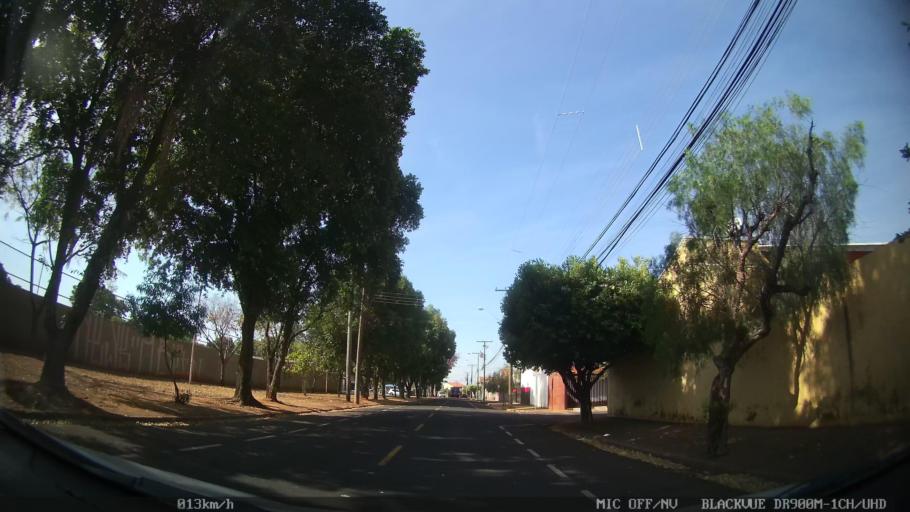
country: BR
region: Sao Paulo
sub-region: Sao Jose Do Rio Preto
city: Sao Jose do Rio Preto
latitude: -20.7936
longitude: -49.4183
